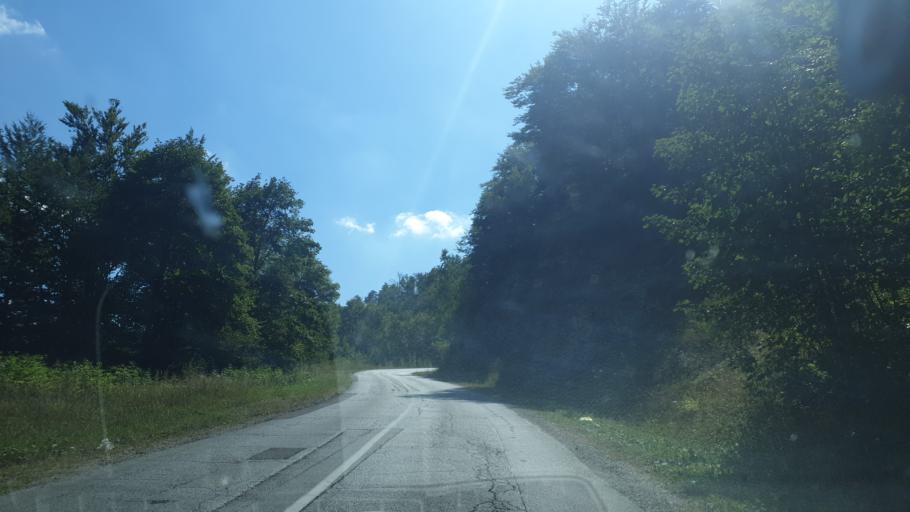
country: RS
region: Central Serbia
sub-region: Kolubarski Okrug
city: Mionica
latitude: 44.1354
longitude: 20.0186
